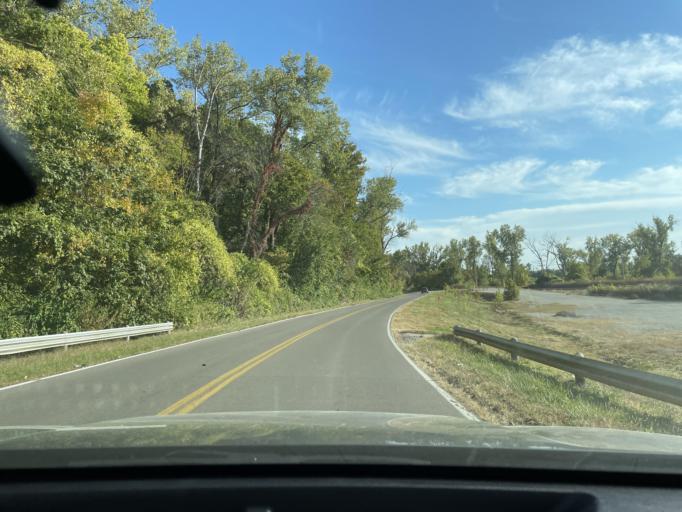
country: US
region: Kansas
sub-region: Doniphan County
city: Elwood
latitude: 39.7798
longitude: -94.8702
